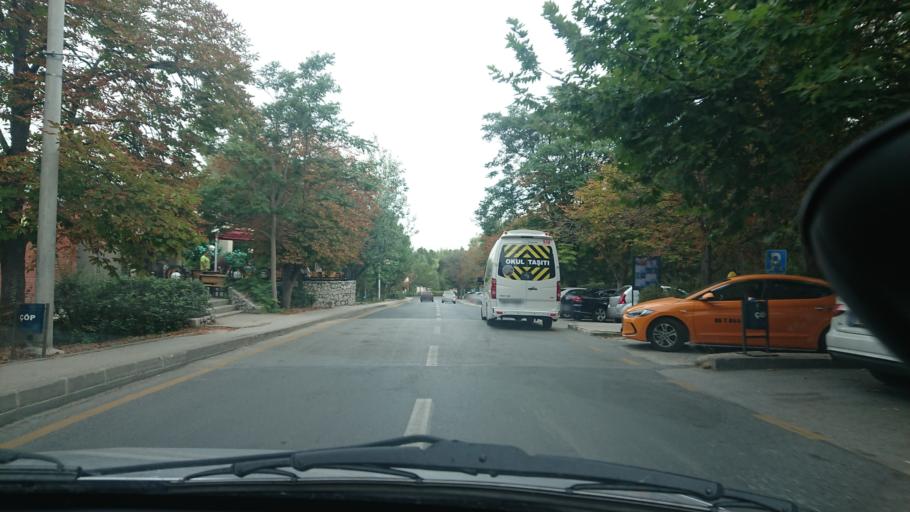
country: TR
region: Ankara
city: Ankara
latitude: 39.8916
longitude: 32.7892
